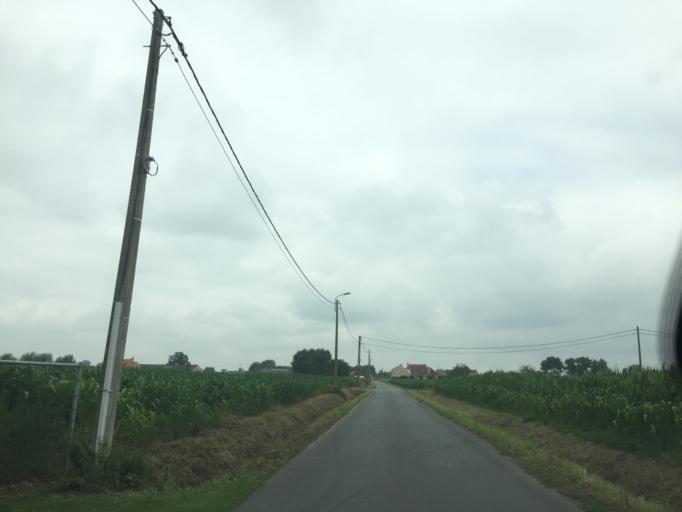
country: BE
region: Flanders
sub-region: Provincie West-Vlaanderen
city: Kortemark
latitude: 51.0055
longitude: 3.0263
